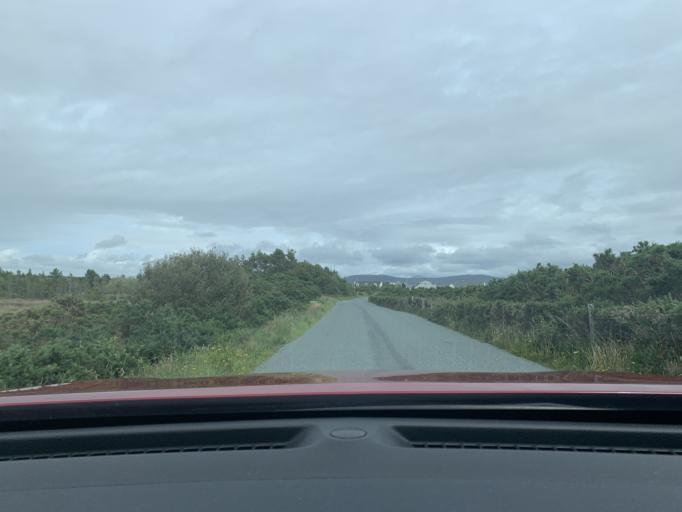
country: IE
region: Ulster
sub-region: County Donegal
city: Dungloe
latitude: 54.9598
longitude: -8.3700
